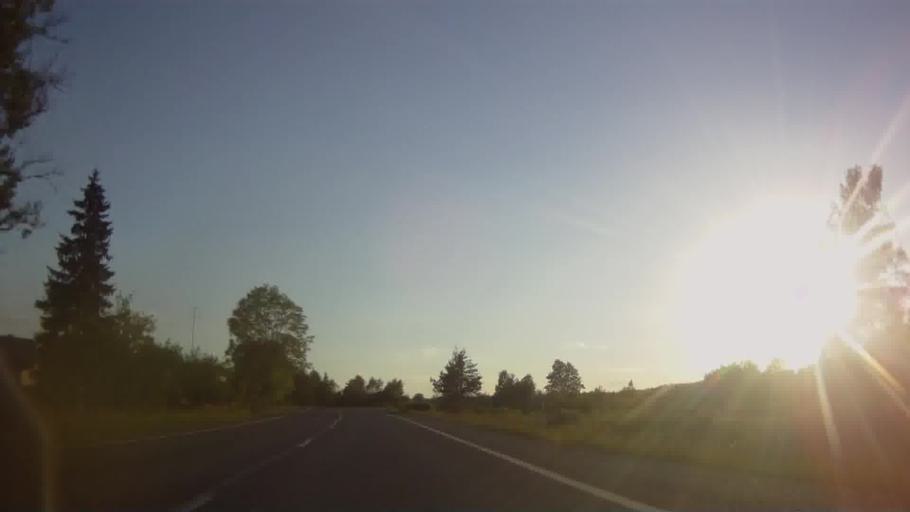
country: LV
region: Livani
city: Livani
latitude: 56.5461
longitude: 26.1066
